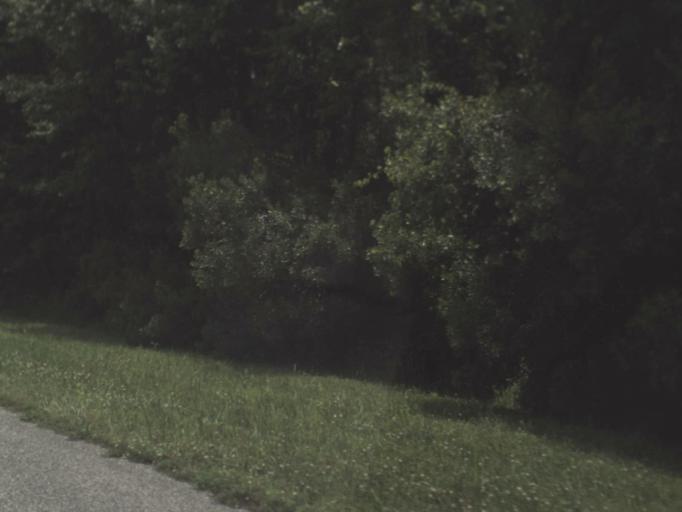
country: US
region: Florida
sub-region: Nassau County
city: Nassau Village-Ratliff
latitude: 30.4663
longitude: -81.7770
